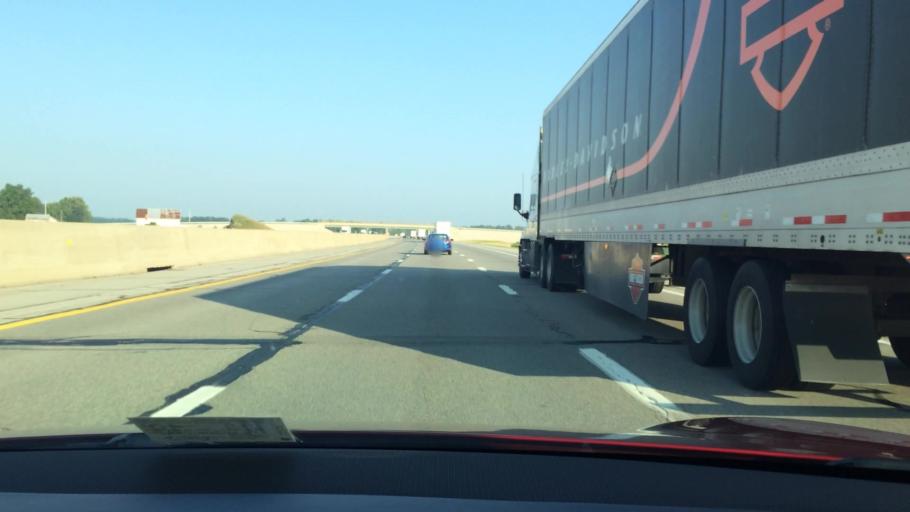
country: US
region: Ohio
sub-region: Sandusky County
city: Stony Prairie
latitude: 41.4216
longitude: -83.1692
